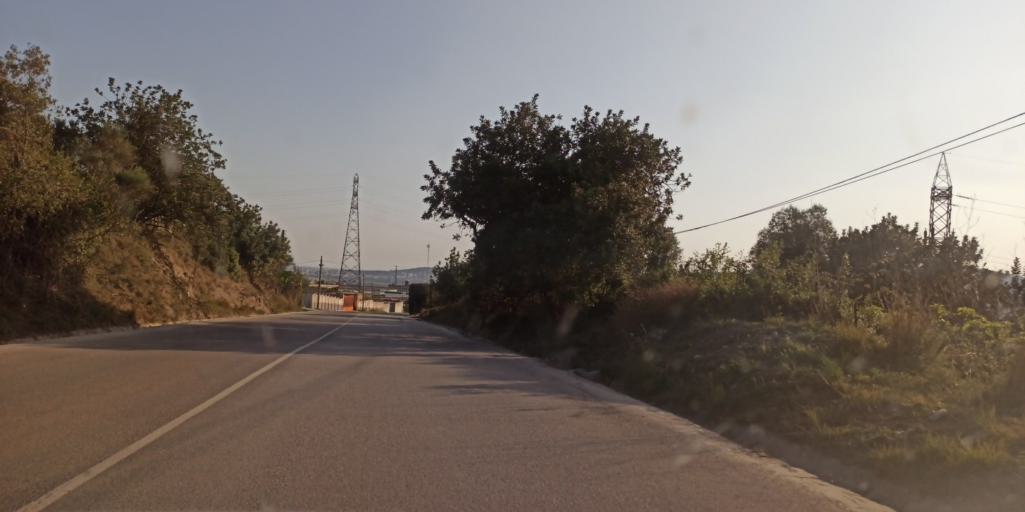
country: ES
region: Catalonia
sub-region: Provincia de Barcelona
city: Sant Feliu de Llobregat
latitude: 41.3963
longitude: 2.0519
